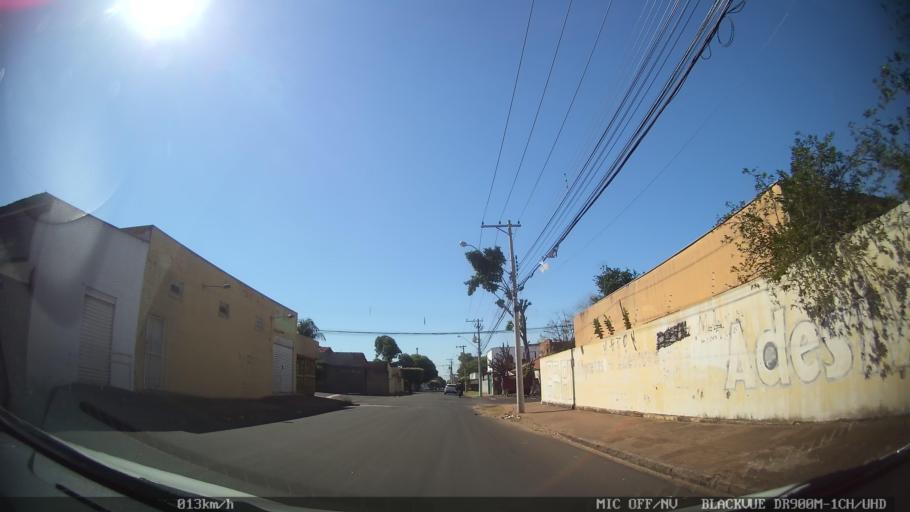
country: BR
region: Sao Paulo
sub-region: Sao Jose Do Rio Preto
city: Sao Jose do Rio Preto
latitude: -20.7707
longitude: -49.4106
